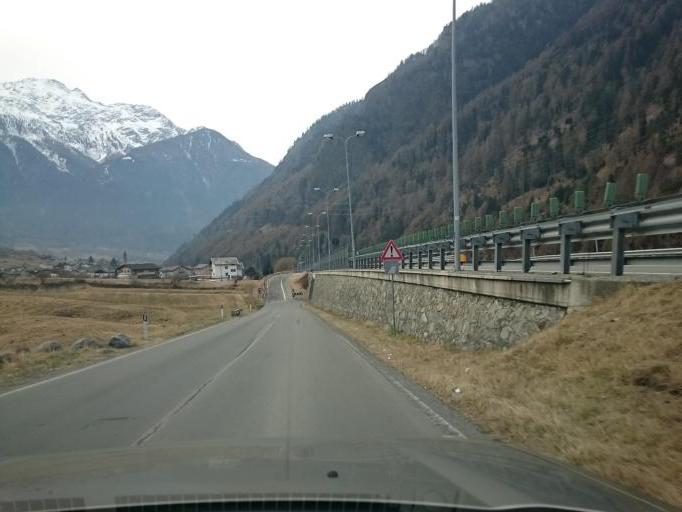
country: IT
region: Lombardy
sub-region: Provincia di Sondrio
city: Sondalo
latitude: 46.3469
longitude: 10.3528
